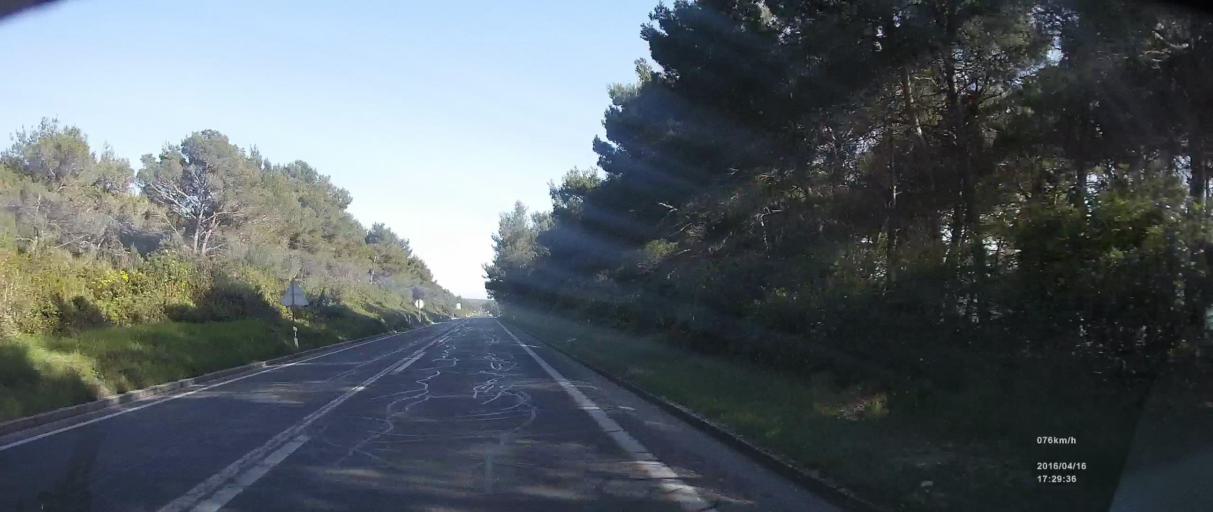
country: HR
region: Zadarska
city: Sukosan
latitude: 44.0298
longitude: 15.3444
